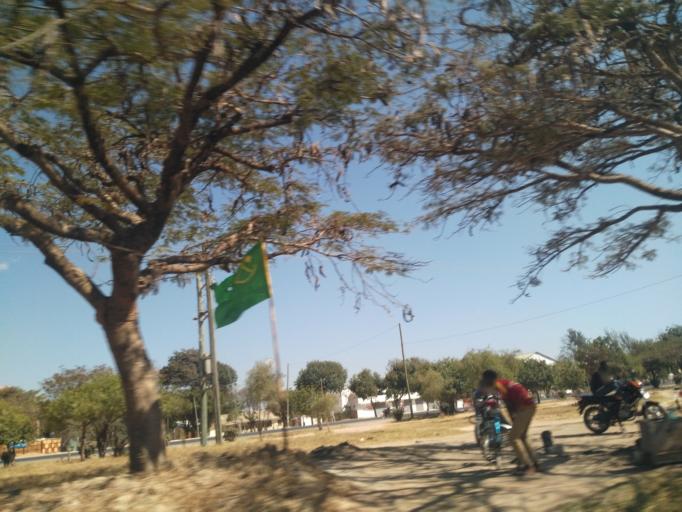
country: TZ
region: Dodoma
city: Dodoma
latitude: -6.1657
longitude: 35.7461
